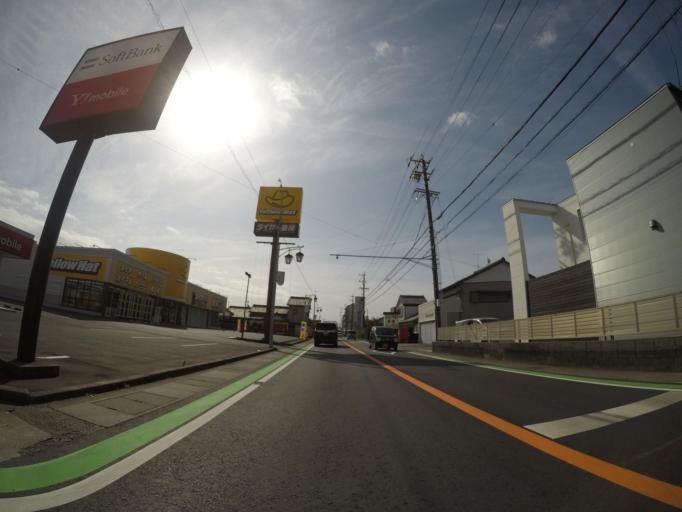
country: JP
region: Shizuoka
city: Hamakita
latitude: 34.7819
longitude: 137.7091
